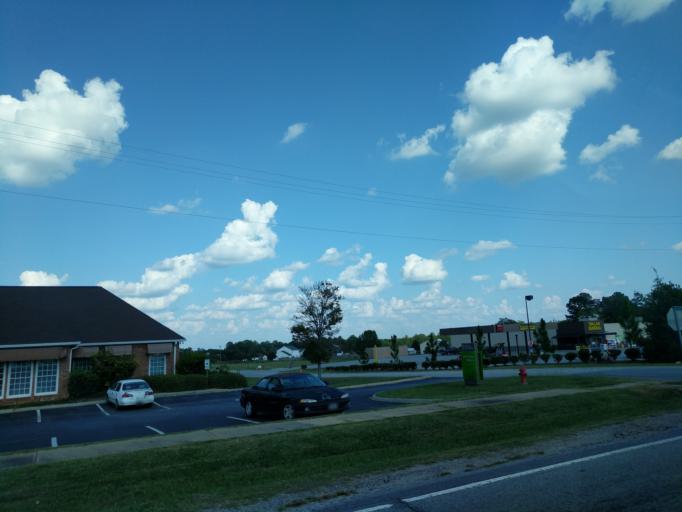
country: US
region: South Carolina
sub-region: Greenville County
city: Fountain Inn
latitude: 34.6180
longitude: -82.1225
